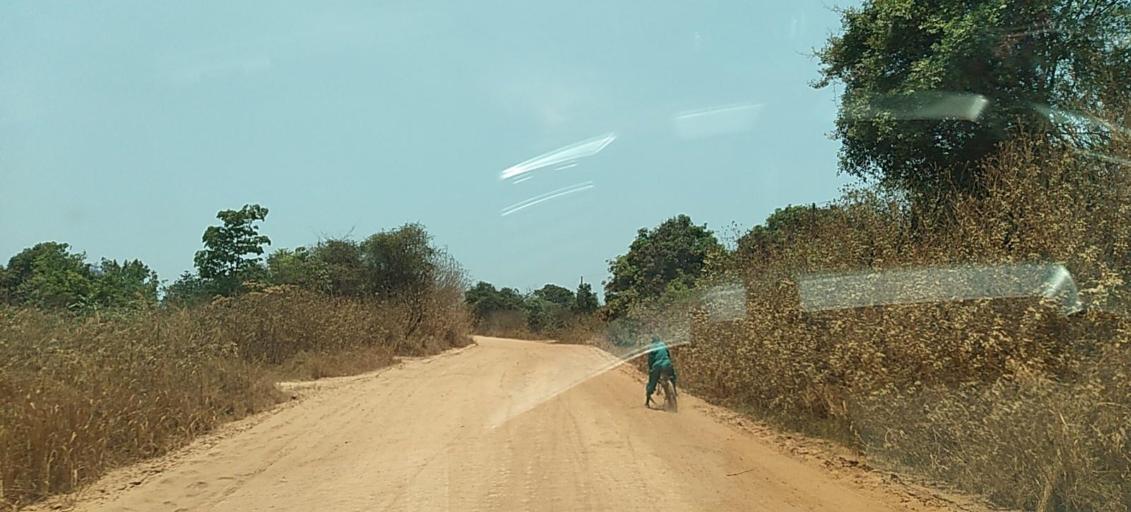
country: CD
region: Katanga
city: Kipushi
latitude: -11.7817
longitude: 27.1831
